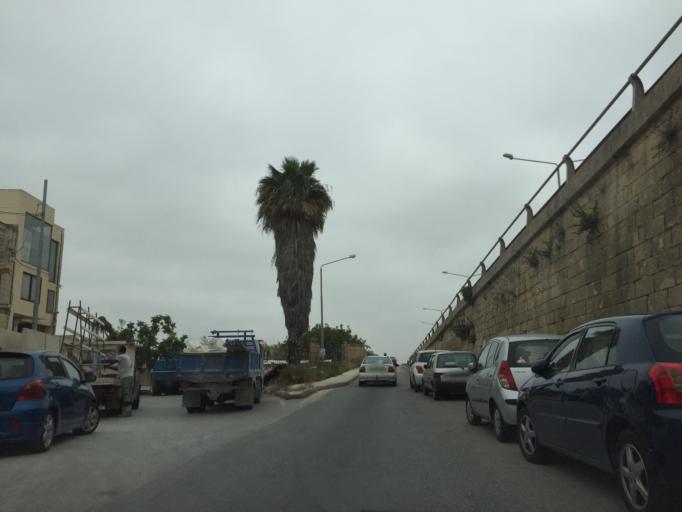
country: MT
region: Saint Venera
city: Santa Venera
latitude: 35.8839
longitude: 14.4728
